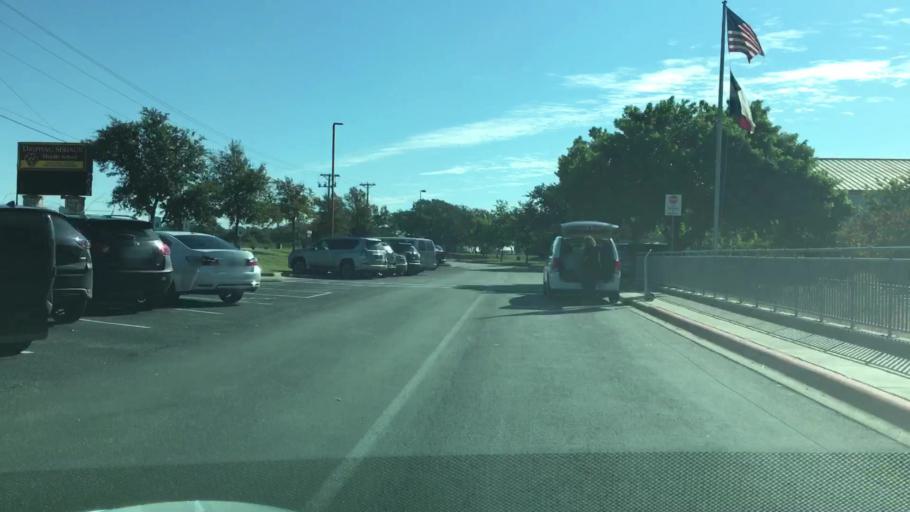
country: US
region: Texas
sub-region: Hays County
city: Dripping Springs
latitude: 30.2027
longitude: -98.1150
